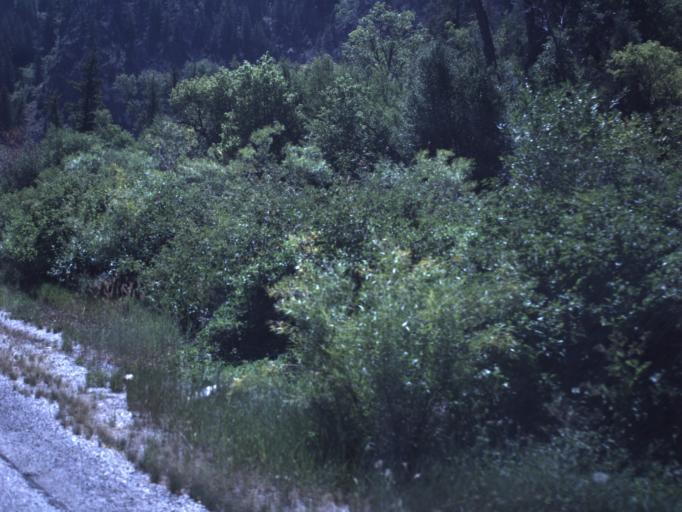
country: US
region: Utah
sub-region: Cache County
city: North Logan
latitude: 41.7923
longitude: -111.6452
